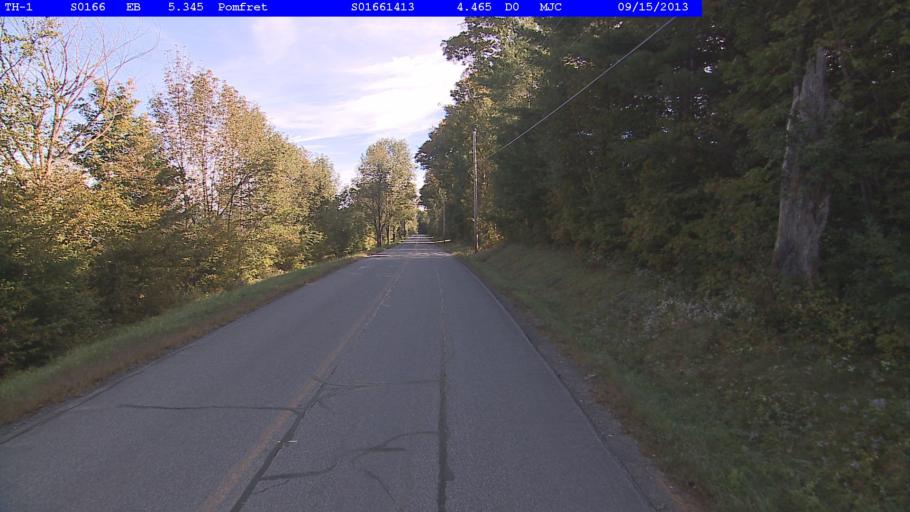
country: US
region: Vermont
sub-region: Windsor County
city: Woodstock
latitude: 43.7066
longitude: -72.5137
